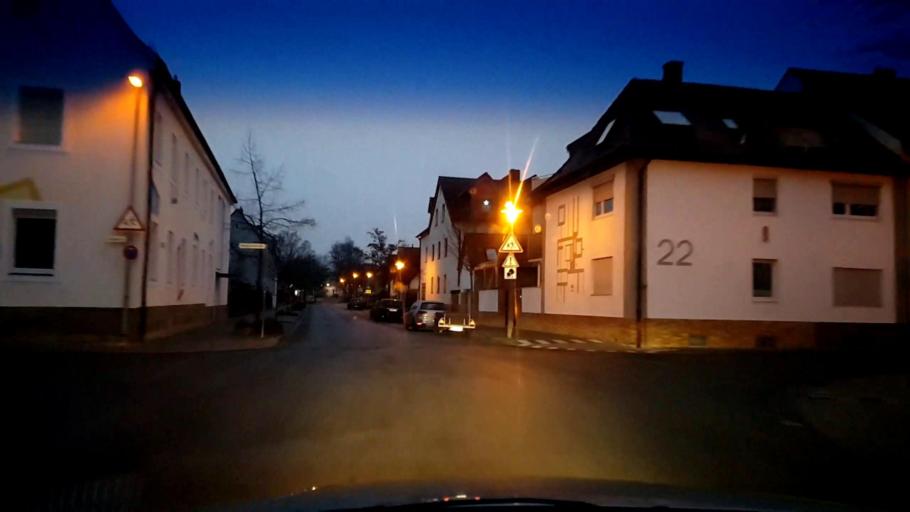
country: DE
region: Bavaria
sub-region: Upper Franconia
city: Hallstadt
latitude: 49.9286
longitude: 10.8781
